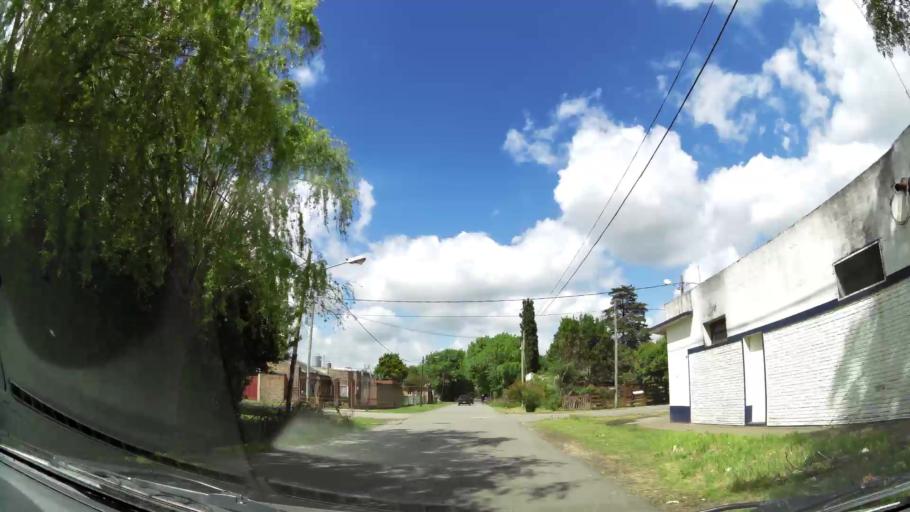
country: AR
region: Buenos Aires
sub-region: Partido de Quilmes
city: Quilmes
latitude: -34.8262
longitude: -58.1882
